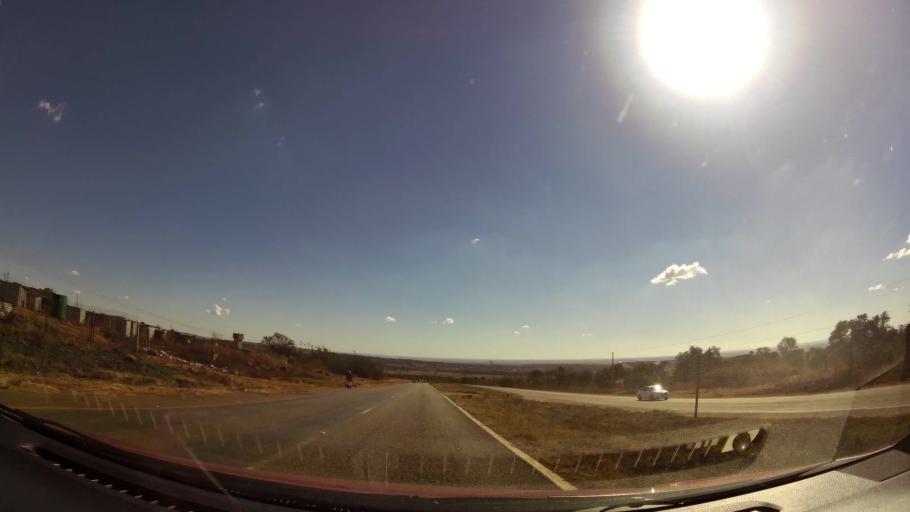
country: ZA
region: Gauteng
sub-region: West Rand District Municipality
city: Carletonville
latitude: -26.4161
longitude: 27.4372
